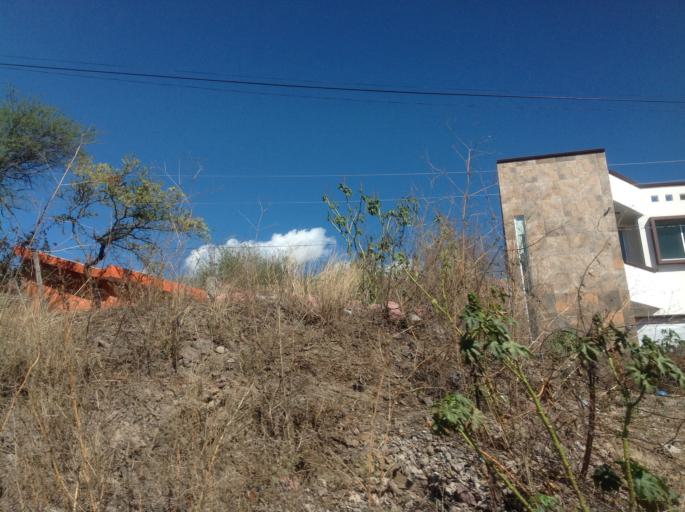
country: MX
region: Oaxaca
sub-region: Heroica Ciudad de Huajuapan de Leon
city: Vista Hermosa
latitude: 17.8154
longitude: -97.7607
